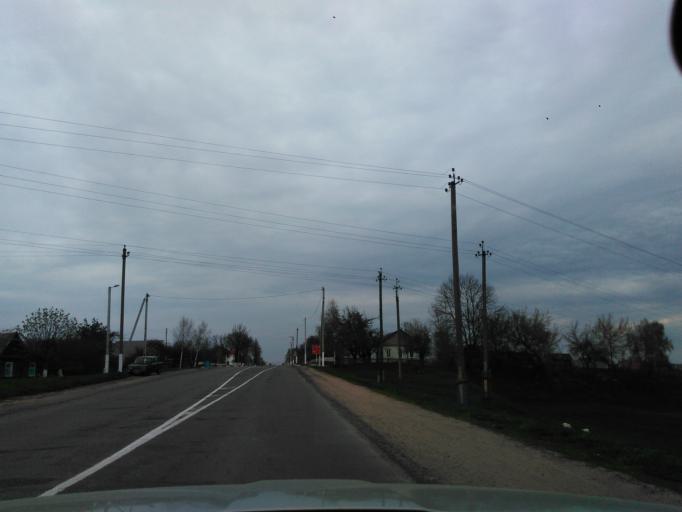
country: BY
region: Vitebsk
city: Chashniki
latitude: 54.8421
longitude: 29.1773
